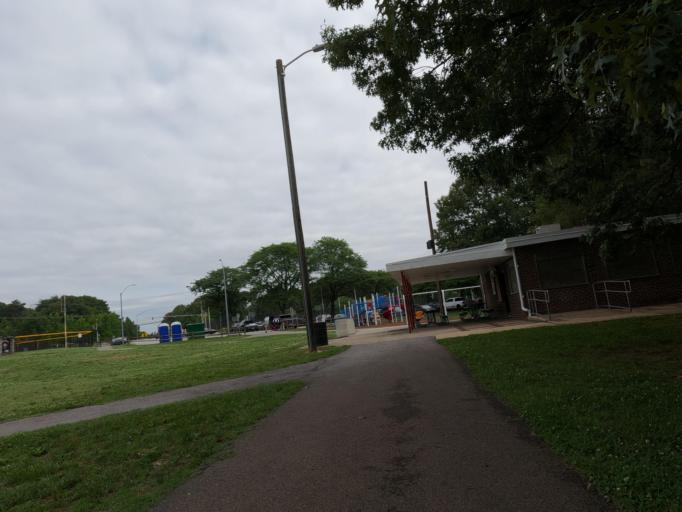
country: US
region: Maryland
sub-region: Anne Arundel County
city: Glen Burnie
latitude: 39.1661
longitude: -76.6379
